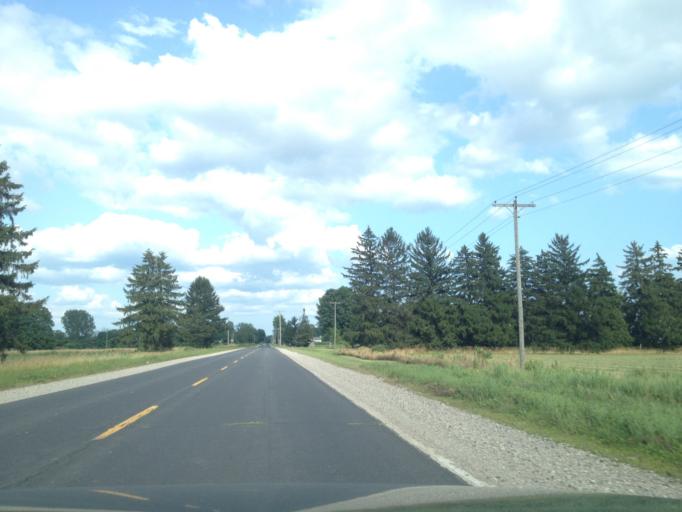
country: CA
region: Ontario
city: Aylmer
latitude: 42.6745
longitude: -80.9180
